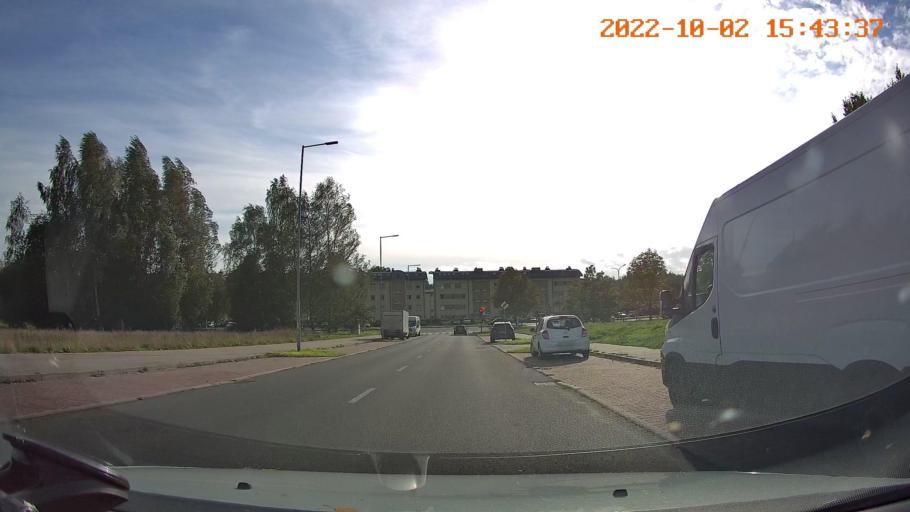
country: PL
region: Silesian Voivodeship
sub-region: Tychy
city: Tychy
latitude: 50.1036
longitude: 18.9826
